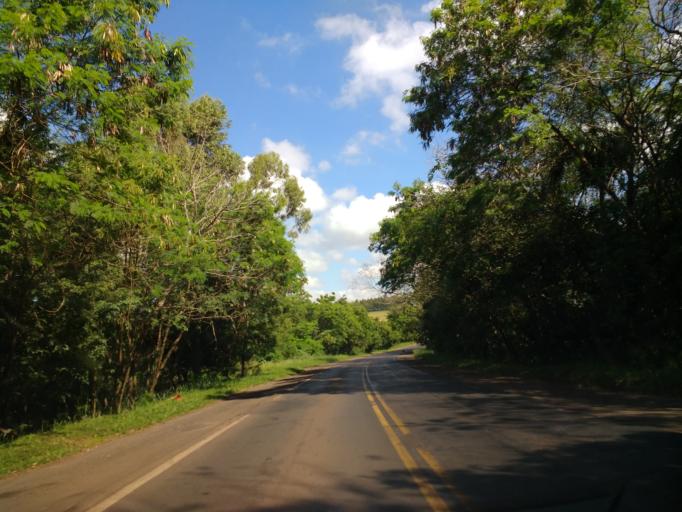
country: BR
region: Parana
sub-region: Umuarama
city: Umuarama
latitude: -23.8792
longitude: -53.3955
